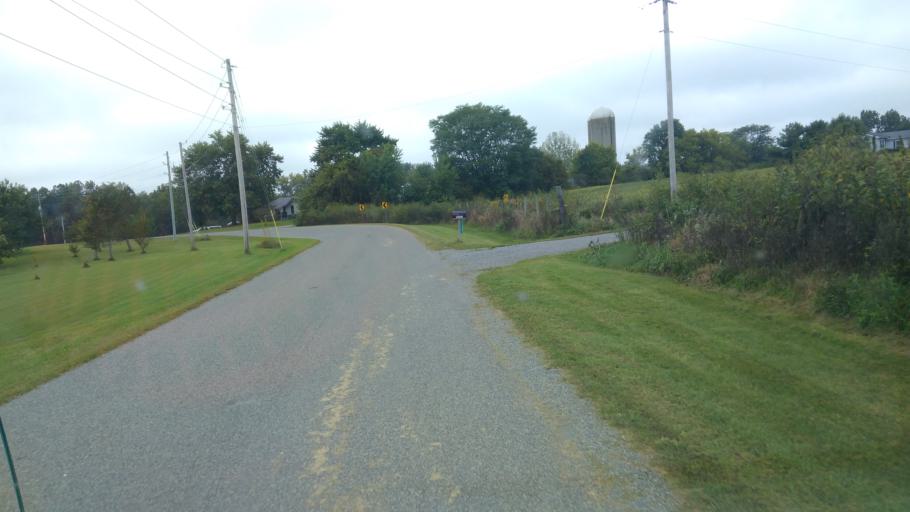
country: US
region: Ohio
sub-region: Hardin County
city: Kenton
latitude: 40.5776
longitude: -83.6638
